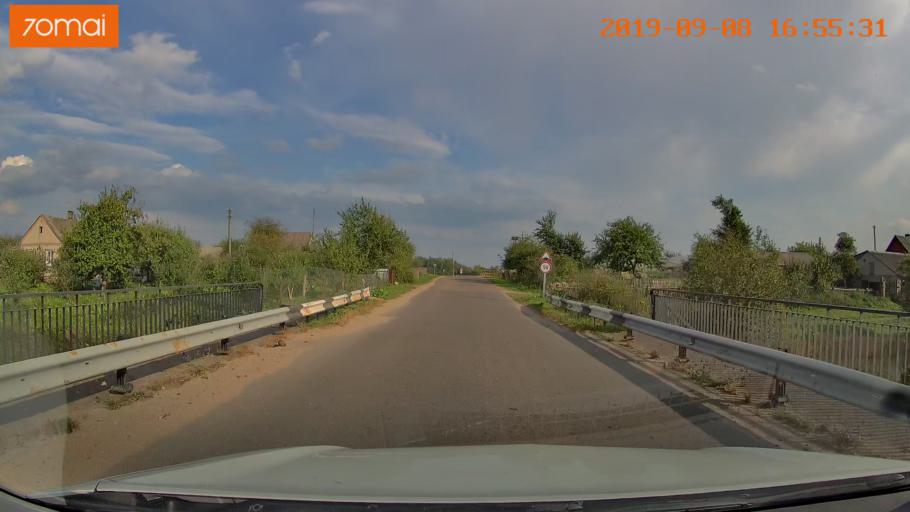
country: BY
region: Grodnenskaya
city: Hrodna
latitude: 53.7479
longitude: 23.9349
